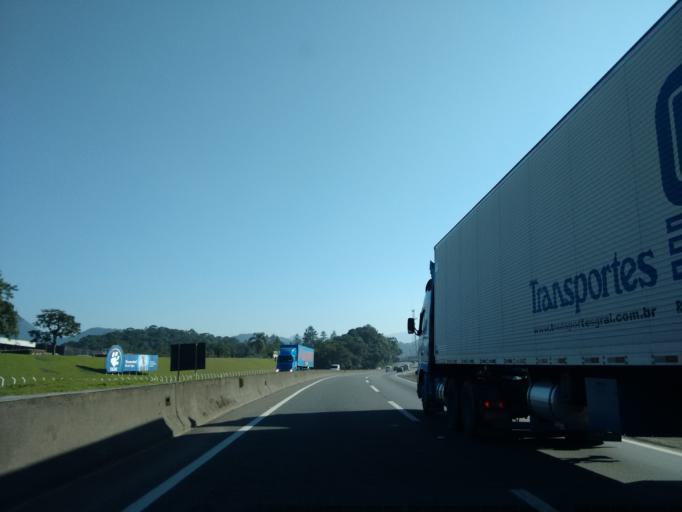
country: BR
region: Santa Catarina
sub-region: Joinville
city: Joinville
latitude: -26.2483
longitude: -48.9097
